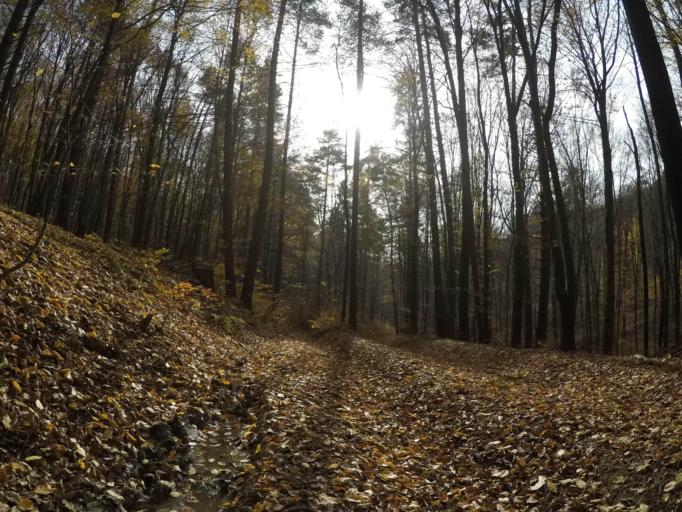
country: SK
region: Presovsky
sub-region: Okres Presov
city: Presov
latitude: 48.9522
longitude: 21.1836
